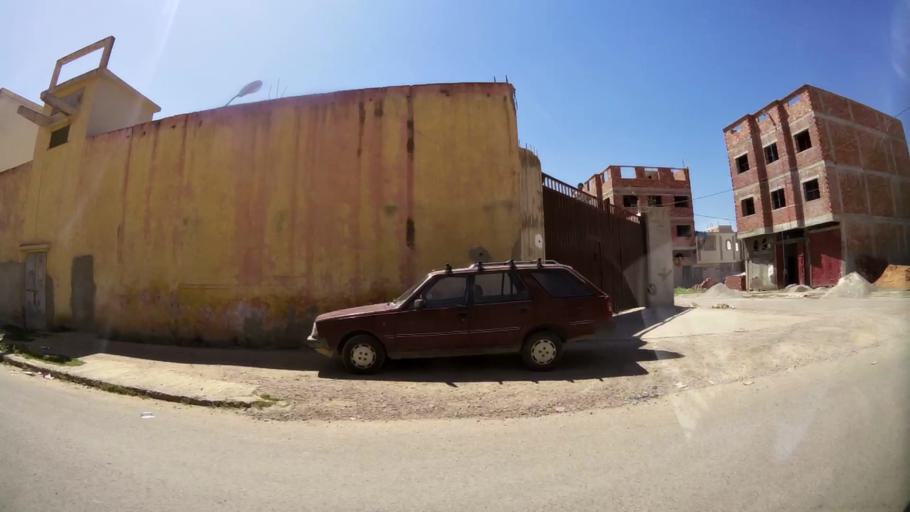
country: MA
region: Oriental
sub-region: Oujda-Angad
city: Oujda
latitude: 34.6895
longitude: -1.9363
